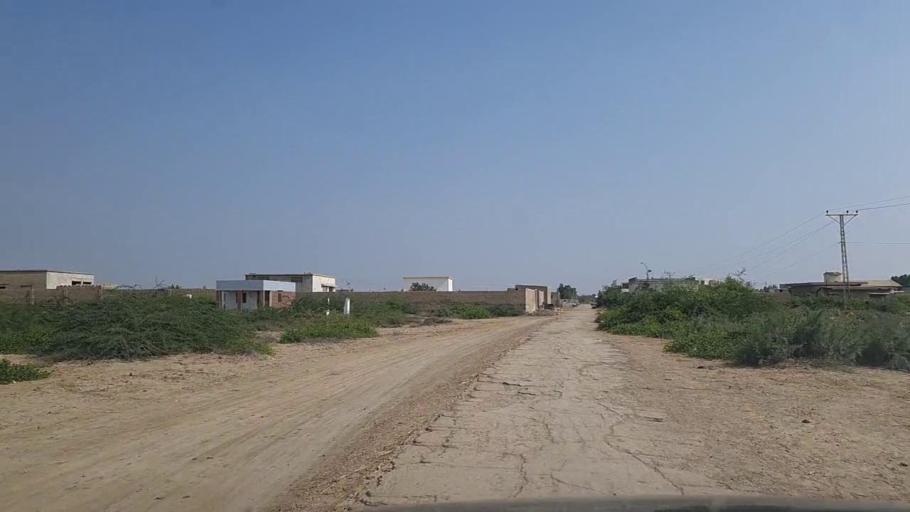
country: PK
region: Sindh
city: Gharo
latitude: 24.7412
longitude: 67.6717
